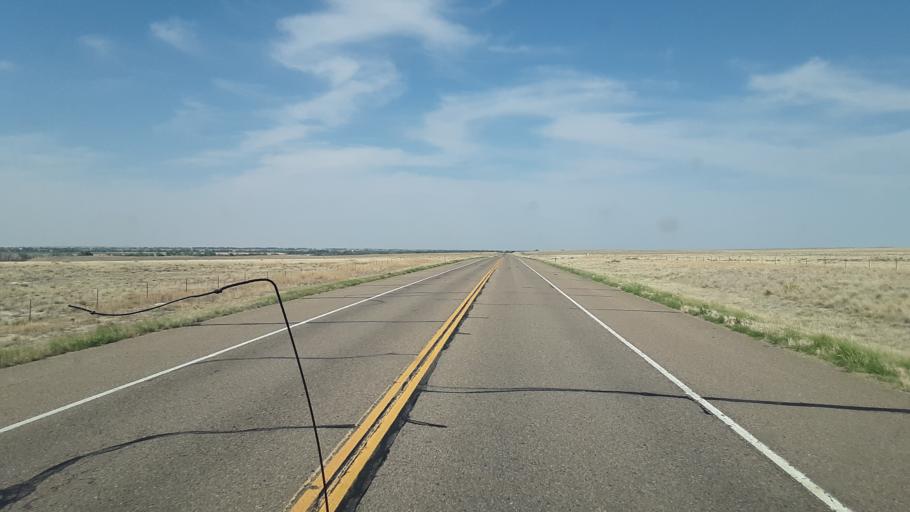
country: US
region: Colorado
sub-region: Bent County
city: Las Animas
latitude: 38.0483
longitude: -103.3660
